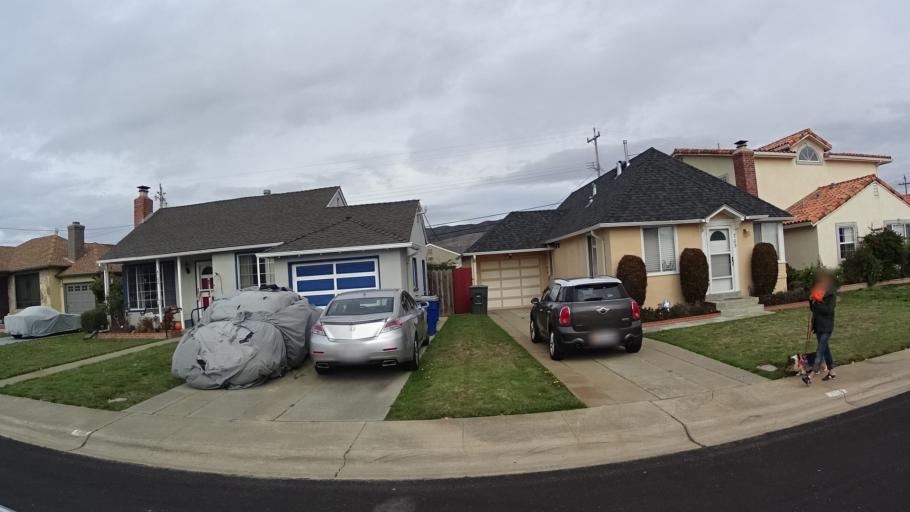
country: US
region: California
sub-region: San Mateo County
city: South San Francisco
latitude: 37.6495
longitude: -122.4324
